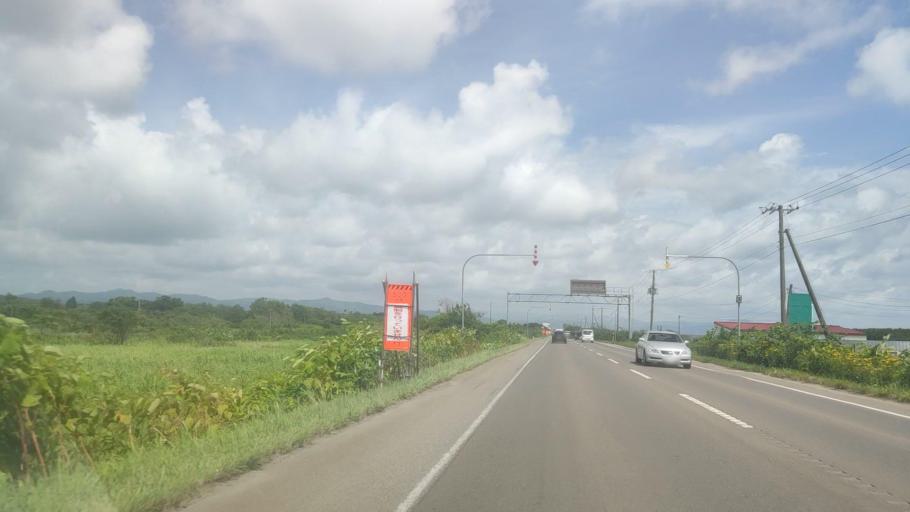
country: JP
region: Hokkaido
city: Niseko Town
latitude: 42.4844
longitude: 140.3529
